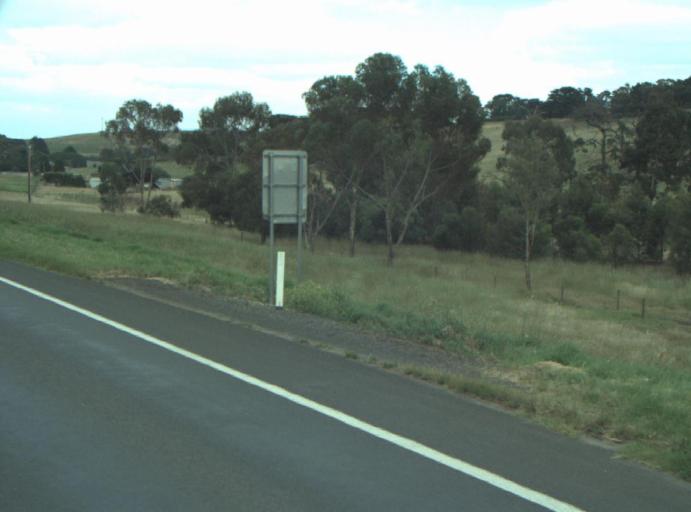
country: AU
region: Victoria
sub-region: Greater Geelong
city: Wandana Heights
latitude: -38.2071
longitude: 144.2857
